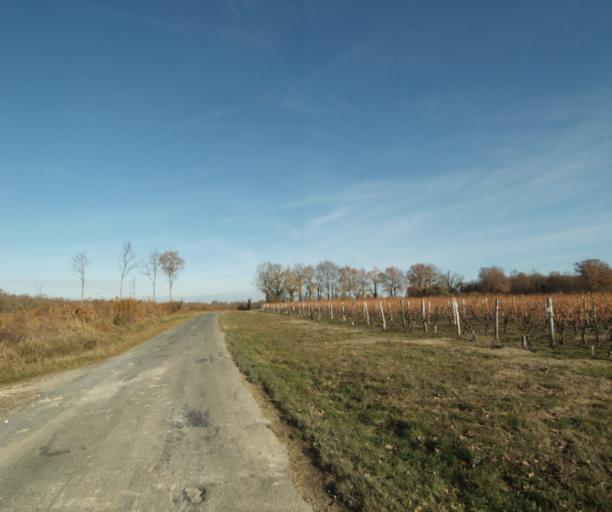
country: FR
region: Poitou-Charentes
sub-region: Departement de la Charente-Maritime
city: Chaniers
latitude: 45.7568
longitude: -0.5119
